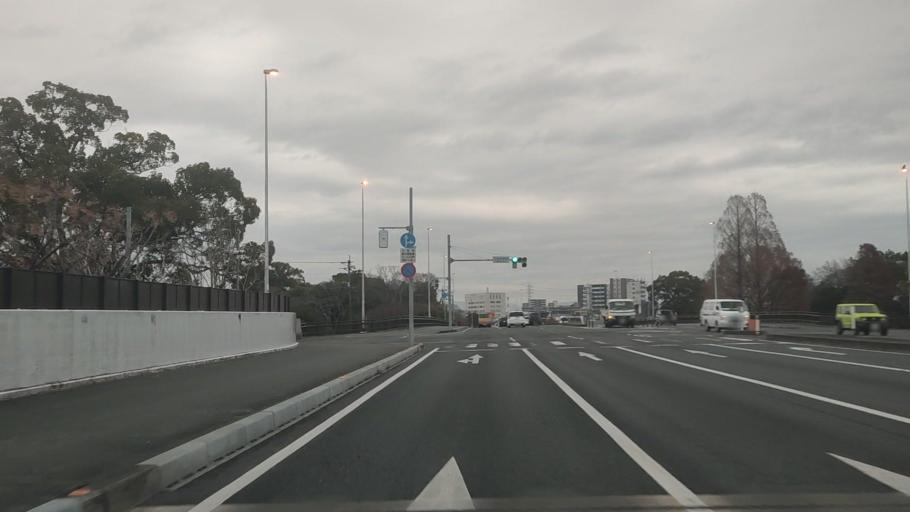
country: JP
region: Kumamoto
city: Kumamoto
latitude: 32.7765
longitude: 130.7386
